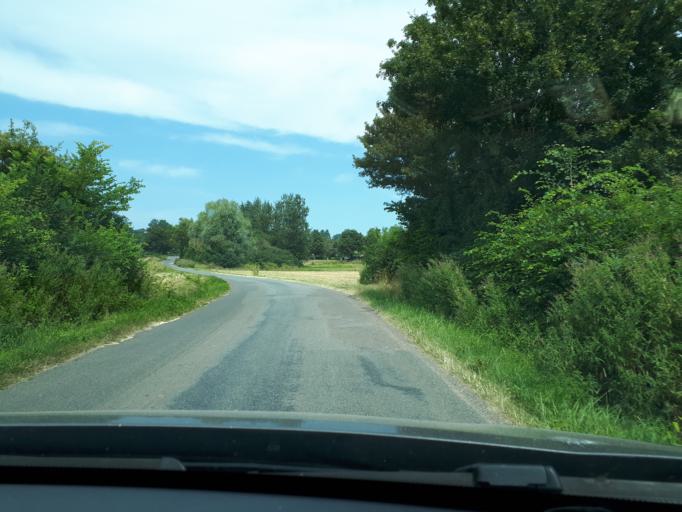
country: FR
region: Centre
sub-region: Departement du Cher
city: Sancerre
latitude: 47.3007
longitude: 2.7476
